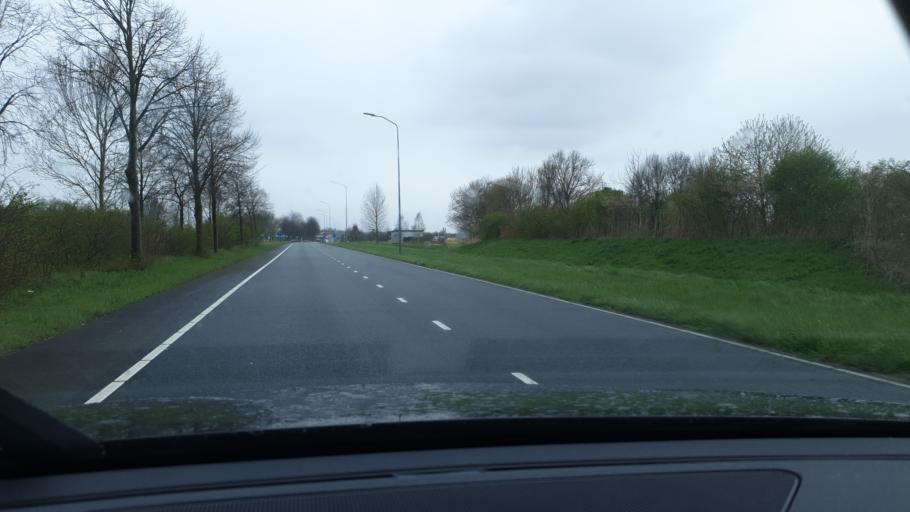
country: NL
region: Flevoland
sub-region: Gemeente Lelystad
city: Lelystad
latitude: 52.4889
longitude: 5.5038
